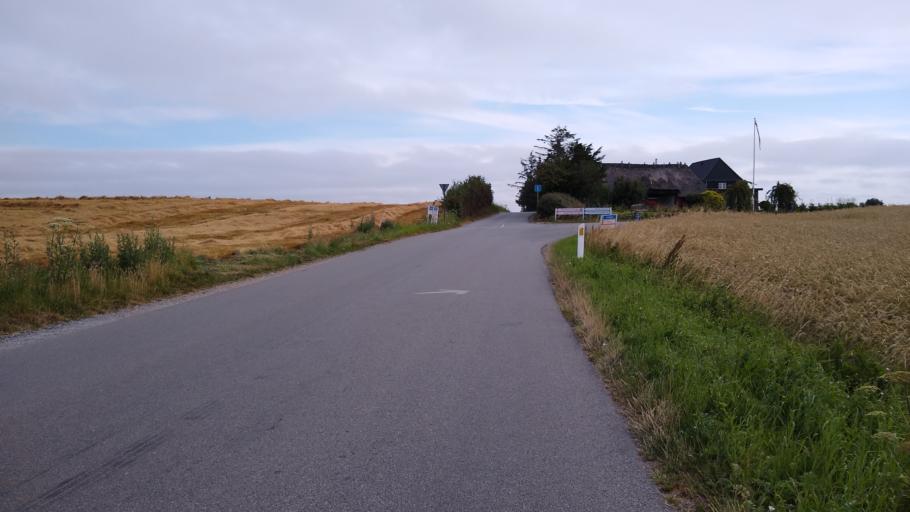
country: DK
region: South Denmark
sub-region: Vejle Kommune
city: Brejning
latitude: 55.6479
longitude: 9.7139
